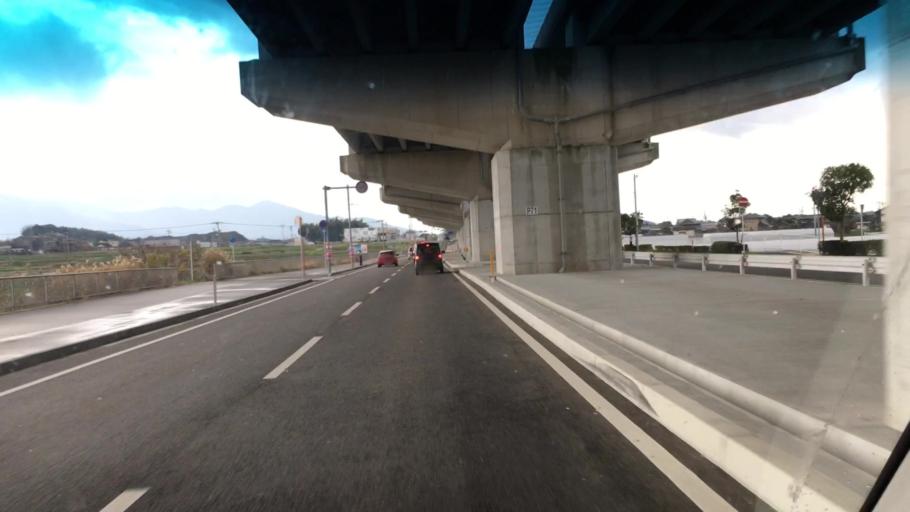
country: JP
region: Fukuoka
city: Maebaru-chuo
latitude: 33.5517
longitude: 130.2206
